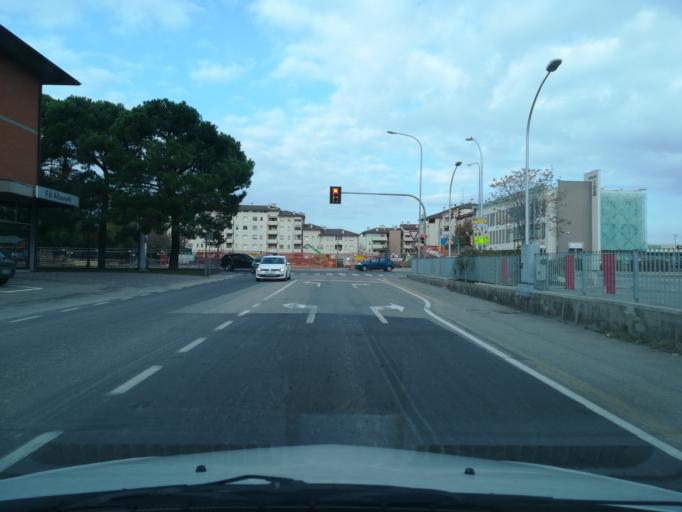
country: IT
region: Emilia-Romagna
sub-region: Provincia di Bologna
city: Imola
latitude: 44.3620
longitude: 11.7249
